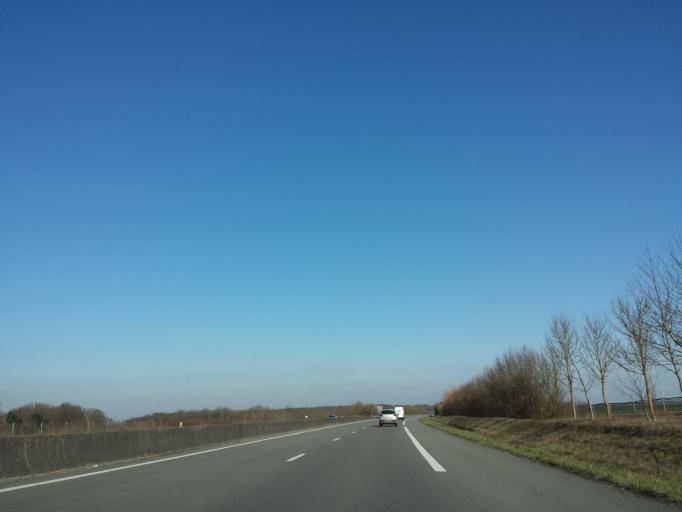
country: FR
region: Picardie
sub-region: Departement de l'Oise
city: Breteuil
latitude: 49.6307
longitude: 2.2090
